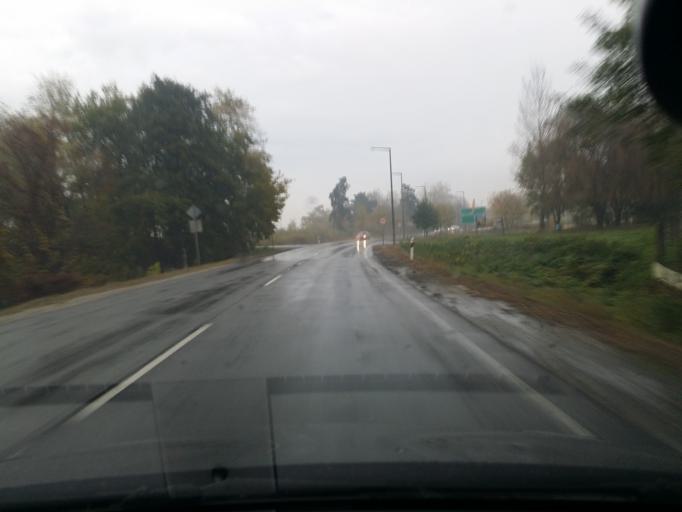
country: HU
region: Szabolcs-Szatmar-Bereg
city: Nyirpazony
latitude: 47.9512
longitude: 21.8171
